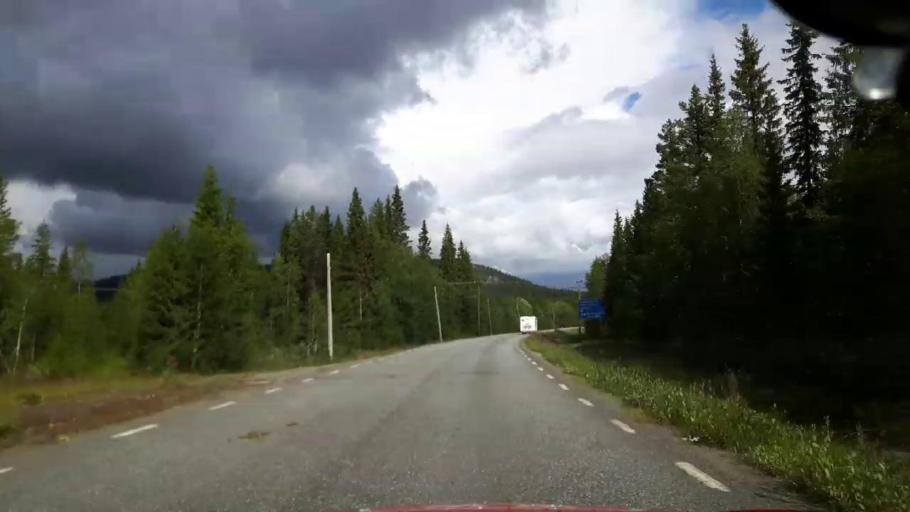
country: SE
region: Vaesterbotten
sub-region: Vilhelmina Kommun
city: Sjoberg
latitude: 64.9332
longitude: 15.8584
